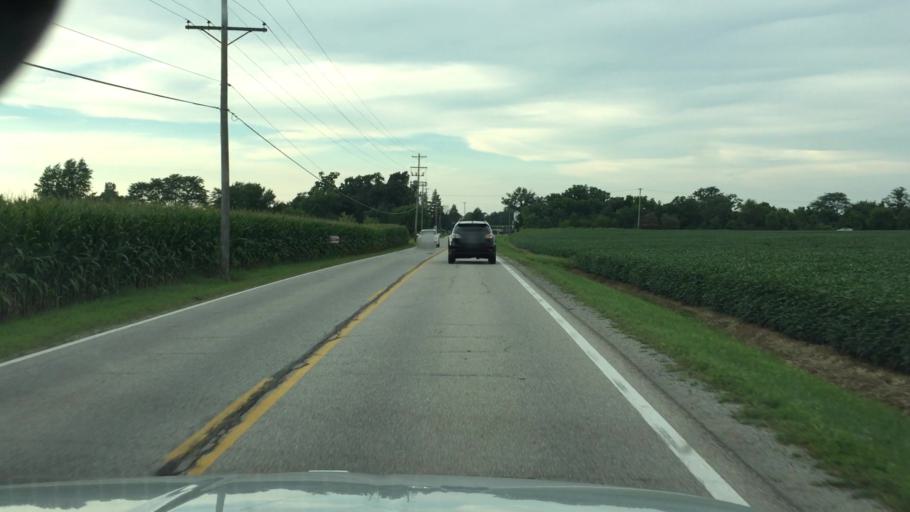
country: US
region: Ohio
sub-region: Madison County
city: Plain City
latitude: 40.0393
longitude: -83.2634
